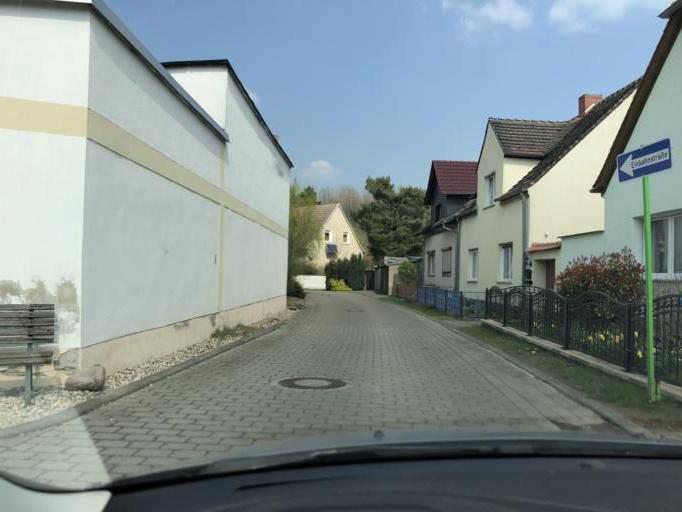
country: DE
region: Saxony-Anhalt
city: Landsberg
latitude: 51.5401
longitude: 12.1357
